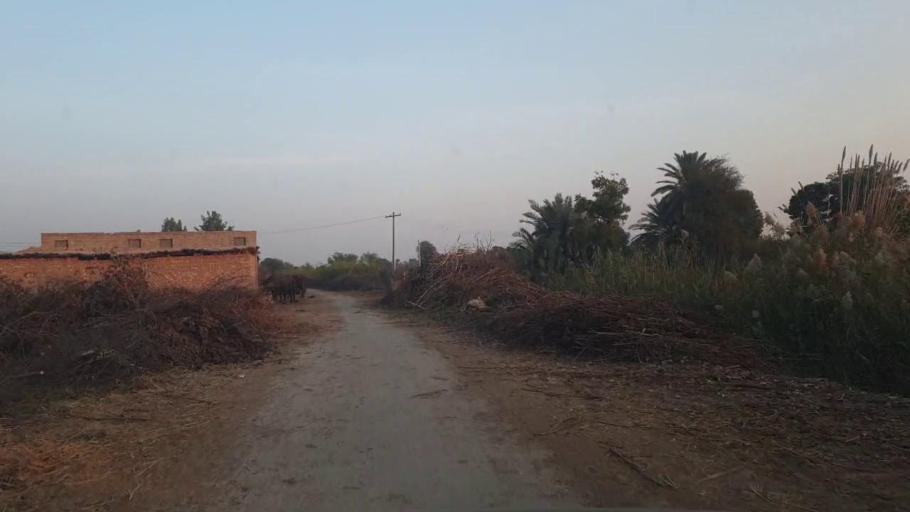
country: PK
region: Sindh
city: Bhit Shah
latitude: 25.8701
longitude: 68.5348
